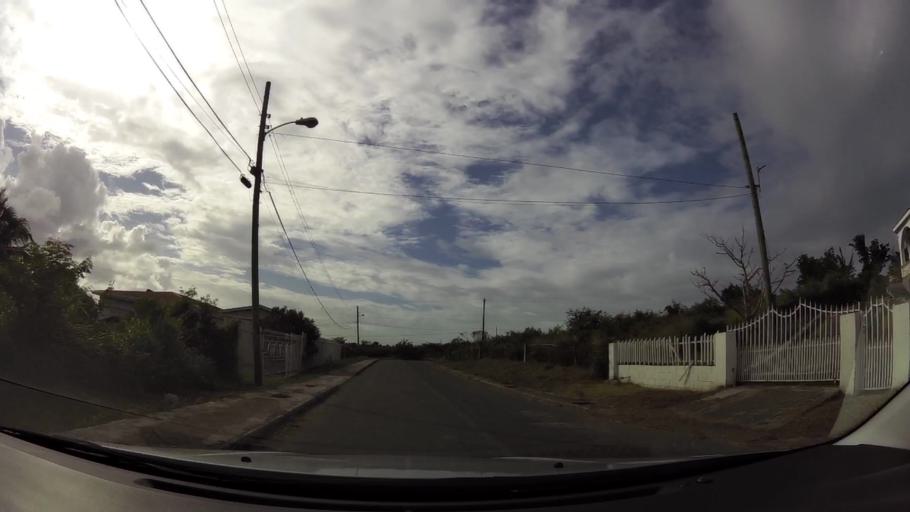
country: AG
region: Saint George
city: Piggotts
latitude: 17.1334
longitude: -61.8216
